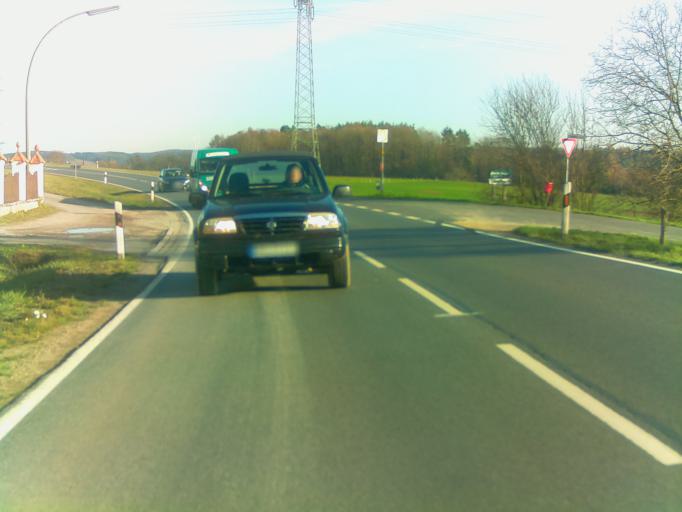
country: DE
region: Bavaria
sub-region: Regierungsbezirk Unterfranken
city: Marktheidenfeld
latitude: 49.8357
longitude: 9.5702
